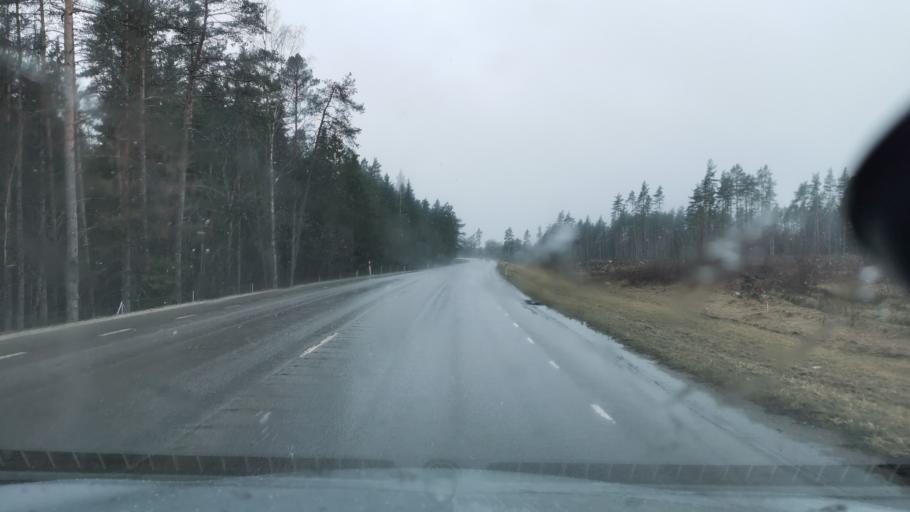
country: EE
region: Harju
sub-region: Kiili vald
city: Kiili
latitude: 59.3154
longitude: 24.7557
